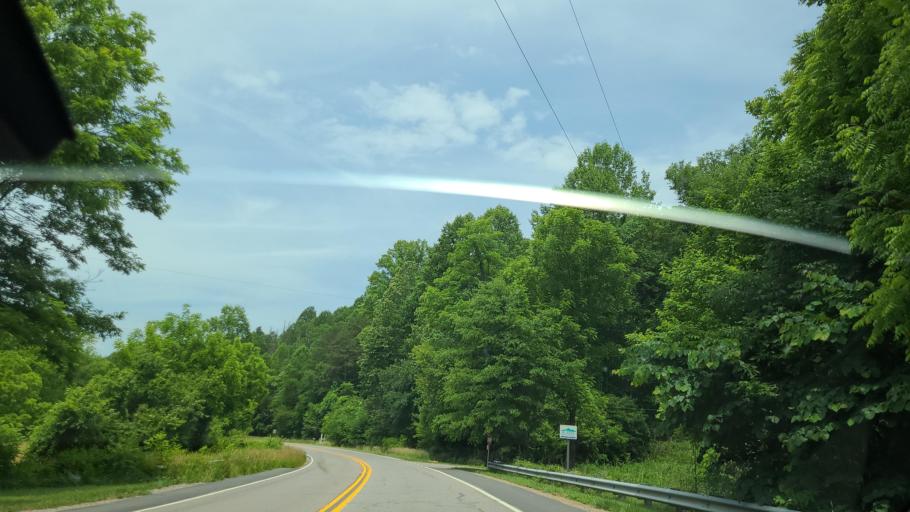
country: US
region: North Carolina
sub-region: Macon County
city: Franklin
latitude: 35.1422
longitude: -83.2884
